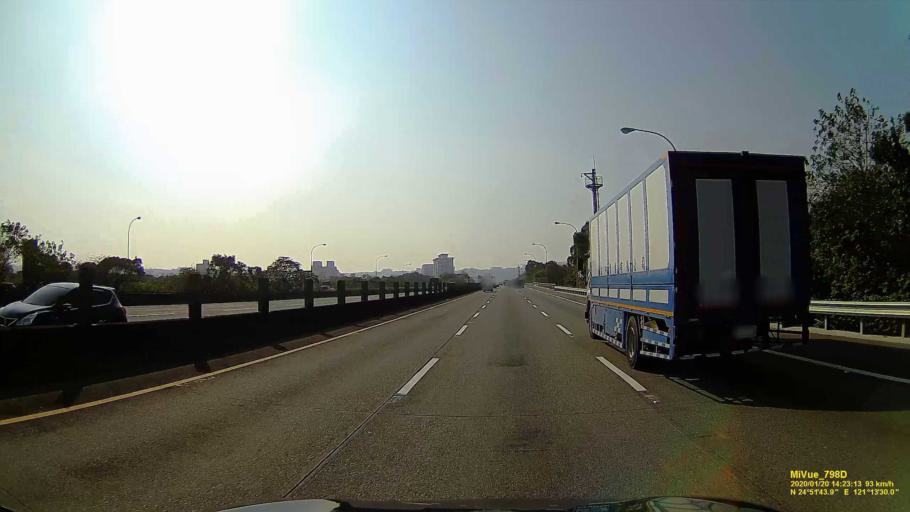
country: TW
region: Taiwan
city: Daxi
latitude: 24.8633
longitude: 121.2257
